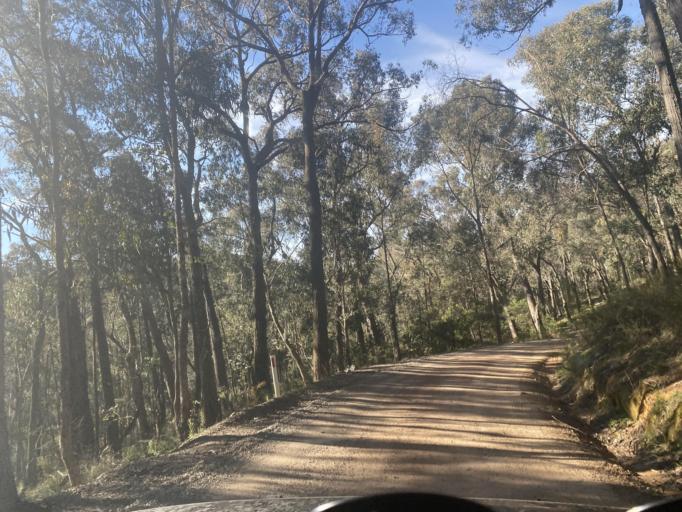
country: AU
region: Victoria
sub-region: Mansfield
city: Mansfield
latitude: -36.8265
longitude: 146.1523
